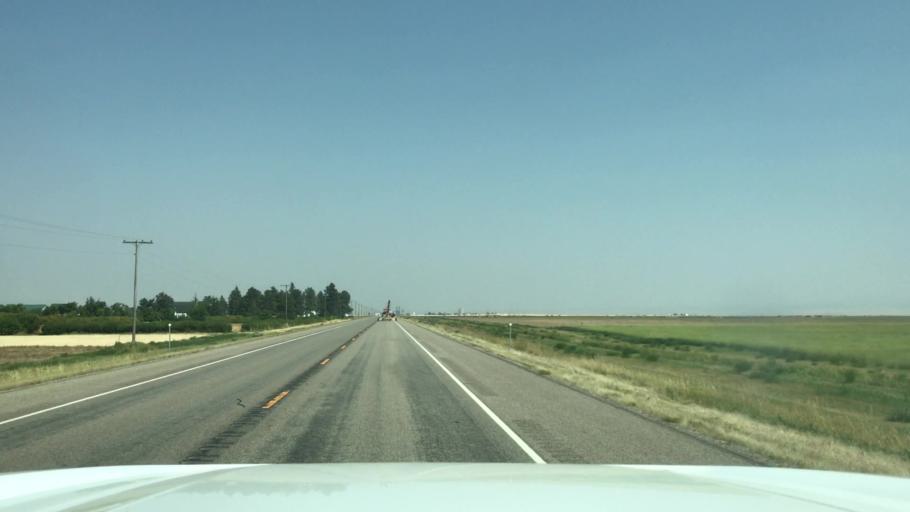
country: US
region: Montana
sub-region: Judith Basin County
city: Stanford
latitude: 47.0551
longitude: -109.9587
